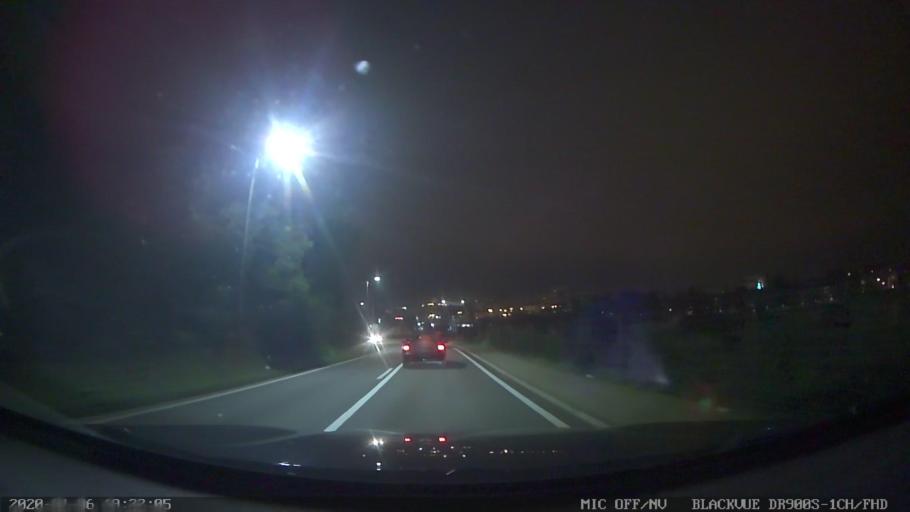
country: PT
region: Vila Real
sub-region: Vila Real
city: Vila Real
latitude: 41.2902
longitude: -7.7332
